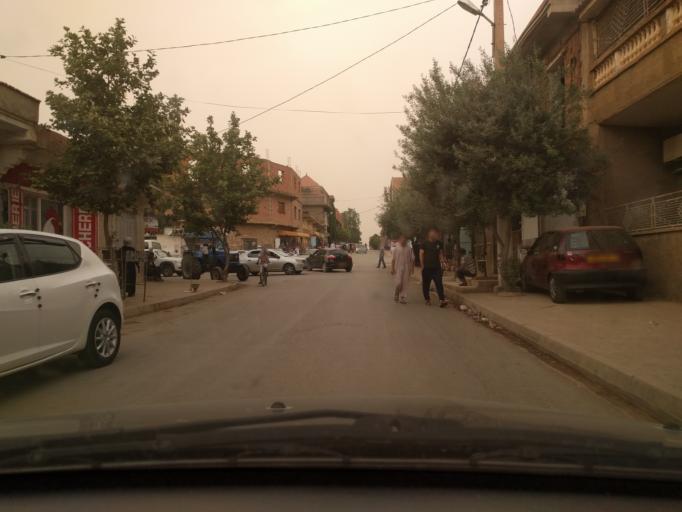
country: DZ
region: Tiaret
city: Frenda
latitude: 35.0650
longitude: 1.0625
